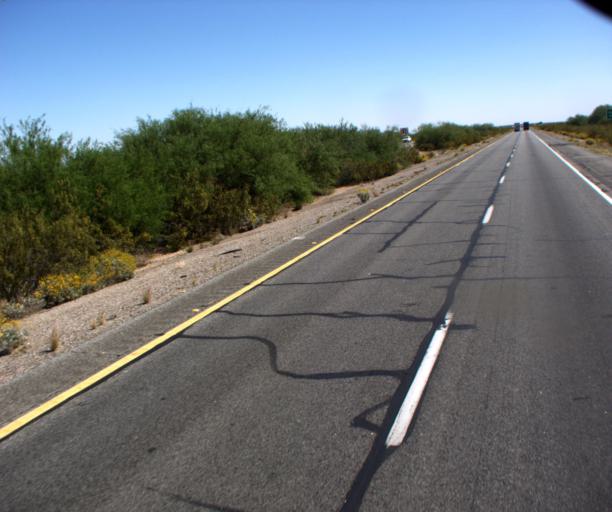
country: US
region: Arizona
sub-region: Maricopa County
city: Buckeye
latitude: 33.4853
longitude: -112.8836
